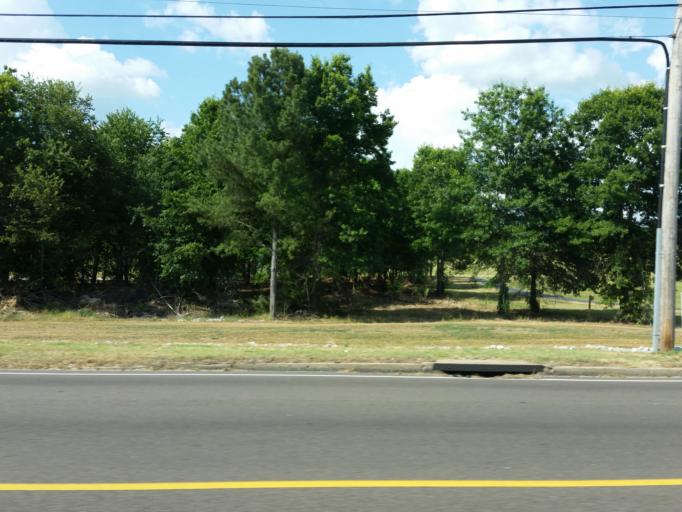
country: US
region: Tennessee
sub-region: Henderson County
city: Lexington
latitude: 35.6587
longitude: -88.4165
